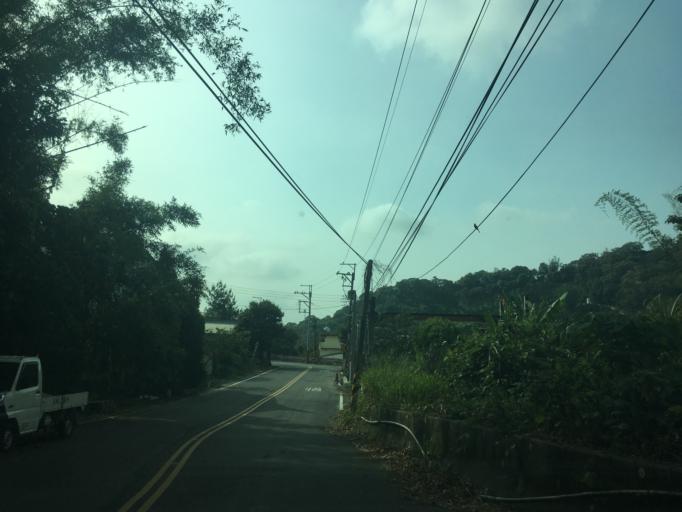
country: TW
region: Taiwan
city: Fengyuan
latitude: 24.2237
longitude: 120.7576
